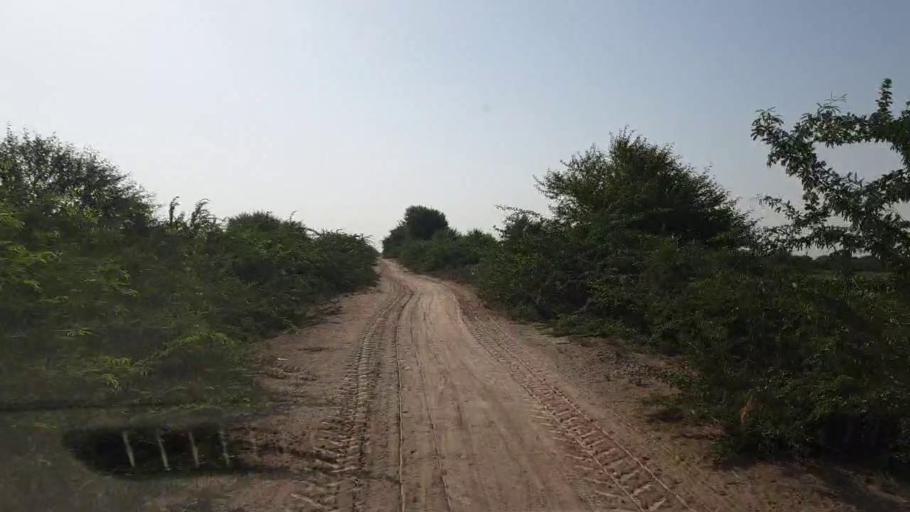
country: PK
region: Sindh
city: Kadhan
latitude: 24.5884
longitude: 69.0774
